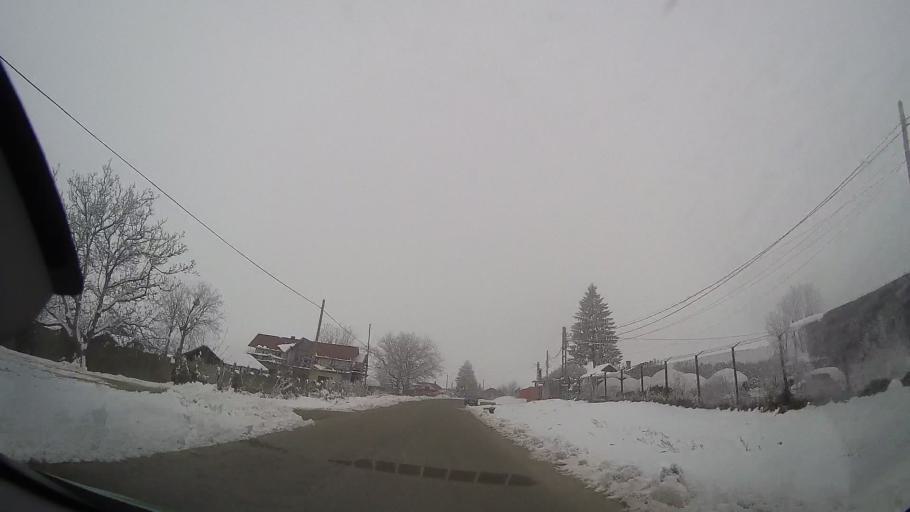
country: RO
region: Neamt
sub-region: Comuna Icusesti
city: Balusesti
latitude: 46.8570
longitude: 27.0266
